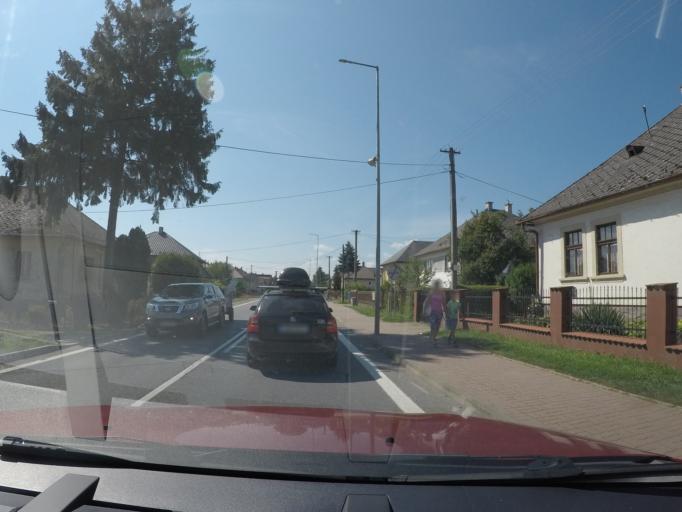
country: SK
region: Presovsky
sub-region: Okres Presov
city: Presov
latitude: 48.9249
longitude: 21.2411
